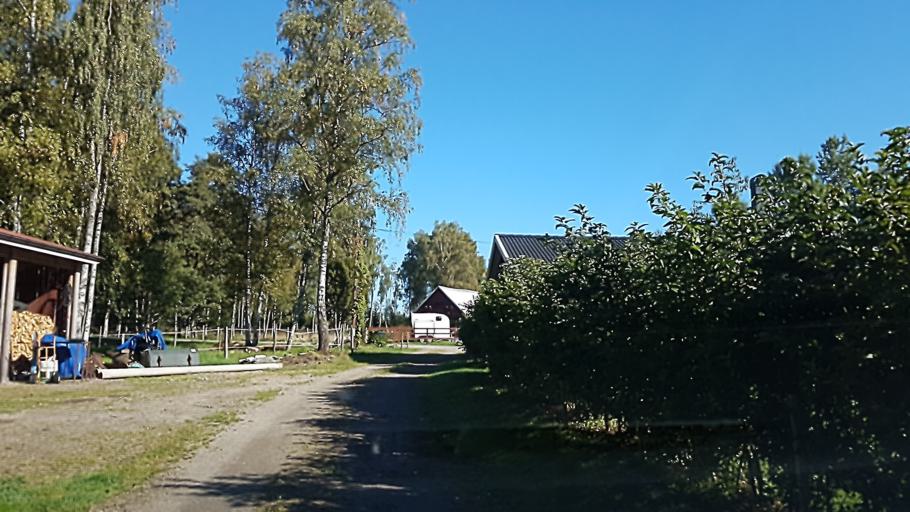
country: SE
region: Kronoberg
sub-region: Ljungby Kommun
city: Ljungby
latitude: 56.8108
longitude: 14.0036
